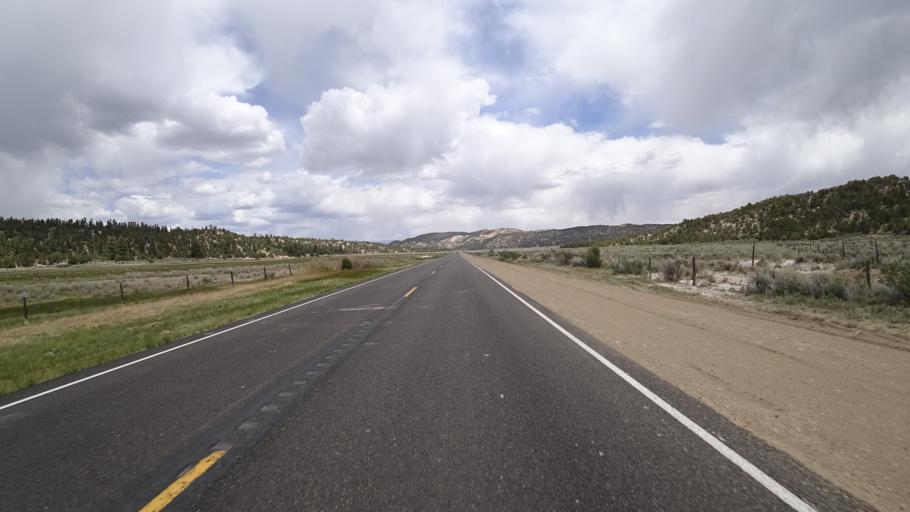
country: US
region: Utah
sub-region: Garfield County
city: Panguitch
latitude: 37.6837
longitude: -111.8114
